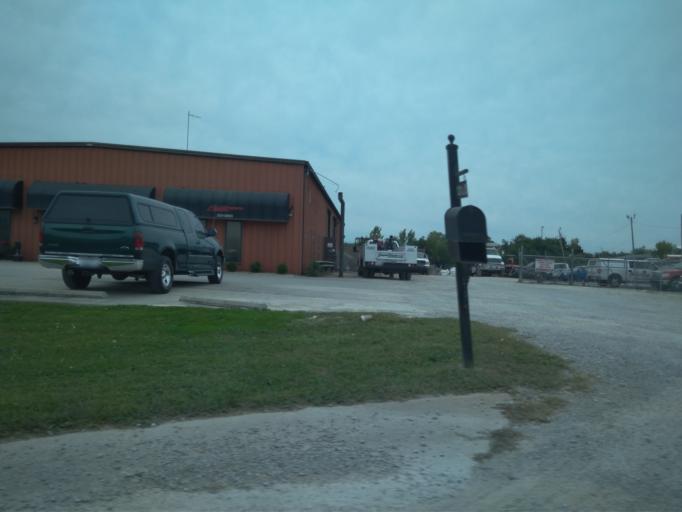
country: US
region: Kentucky
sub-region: Jefferson County
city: Anchorage
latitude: 38.2548
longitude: -85.5064
